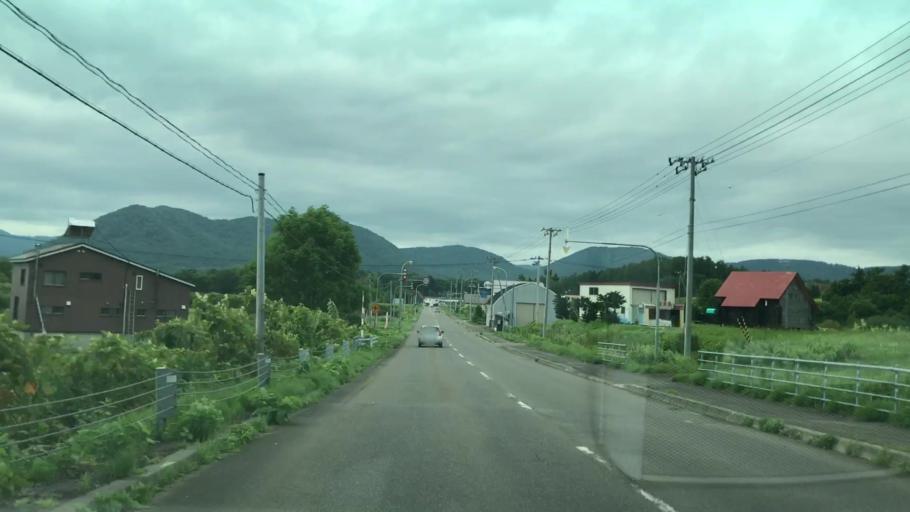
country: JP
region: Hokkaido
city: Yoichi
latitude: 43.0935
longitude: 140.8192
